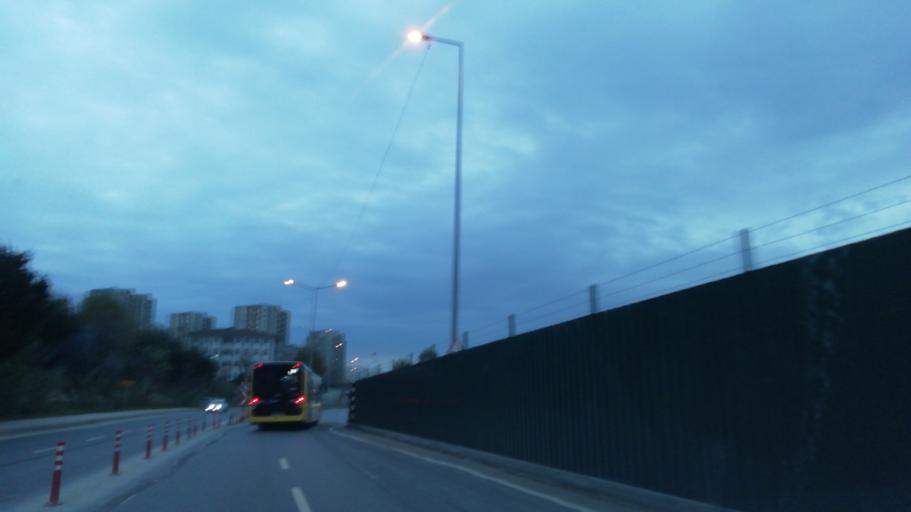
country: TR
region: Istanbul
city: Basaksehir
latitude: 41.0556
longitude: 28.7747
